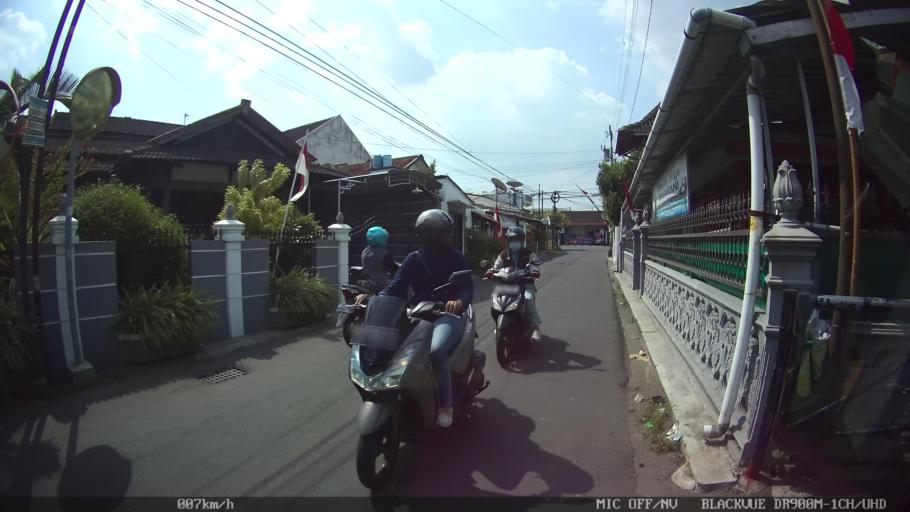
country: ID
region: Daerah Istimewa Yogyakarta
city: Yogyakarta
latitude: -7.8201
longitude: 110.3963
